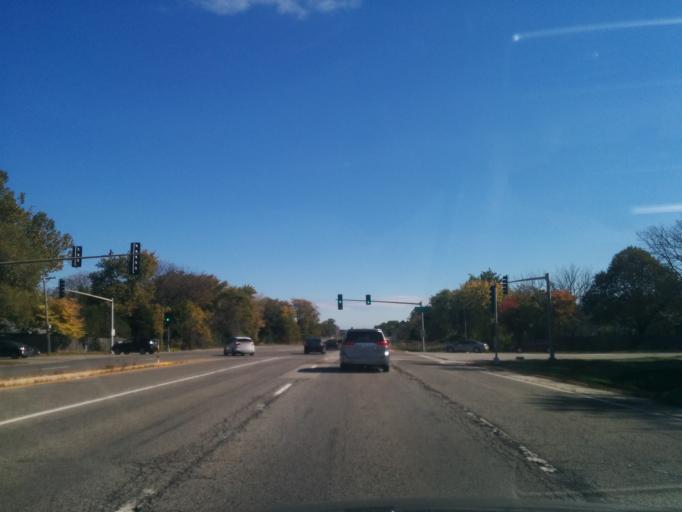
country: US
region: Illinois
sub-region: DuPage County
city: Lisle
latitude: 41.8302
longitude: -88.0783
